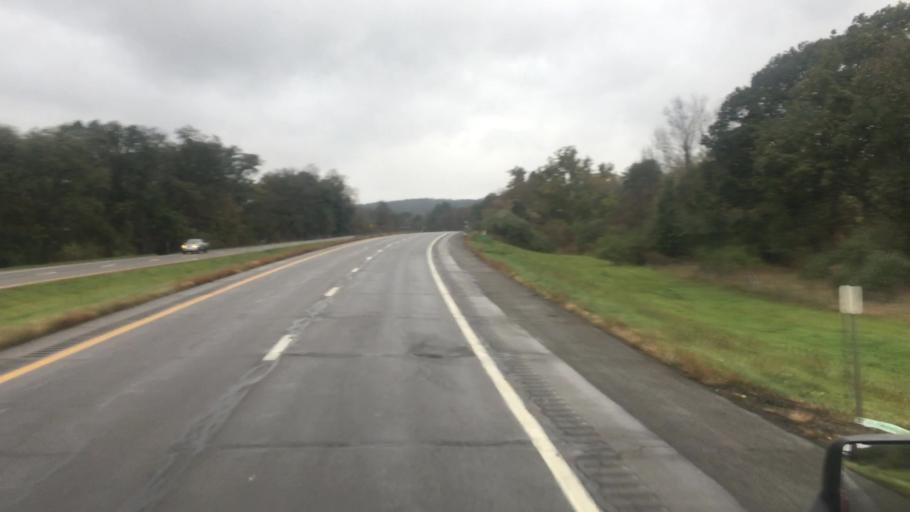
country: US
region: New York
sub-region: Tioga County
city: Apalachin
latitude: 42.0766
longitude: -76.1560
